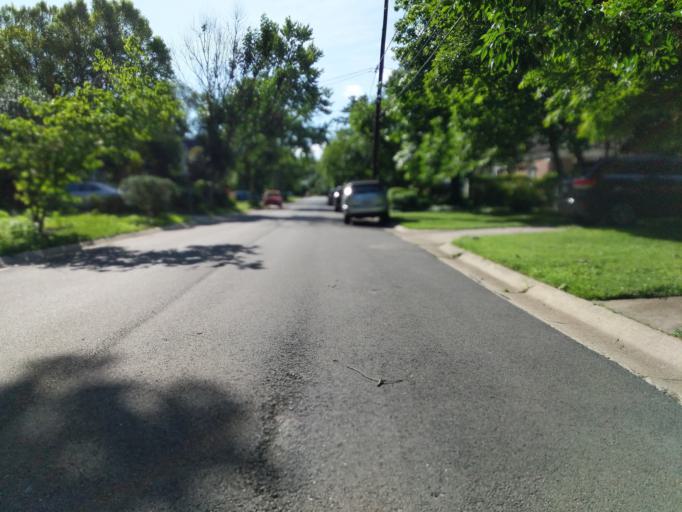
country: US
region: Maryland
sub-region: Montgomery County
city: Bethesda
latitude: 39.0028
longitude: -77.1197
